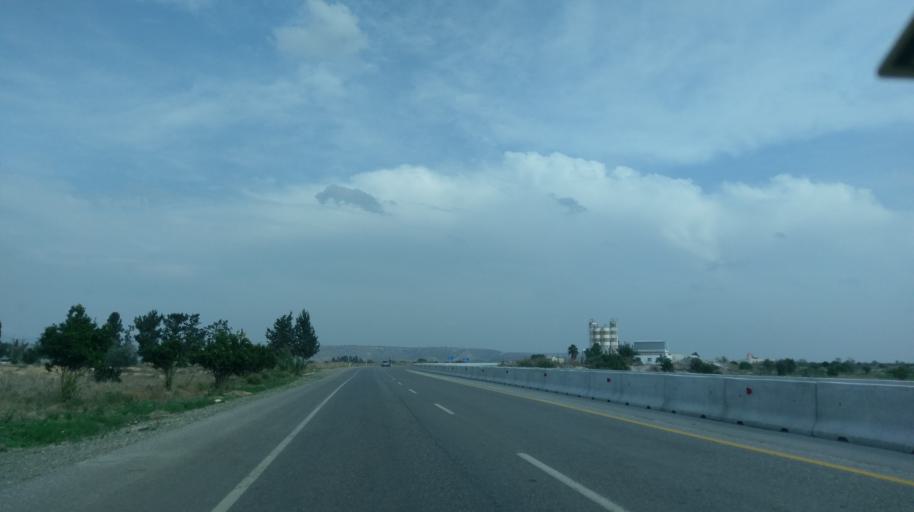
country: CY
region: Lefkosia
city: Morfou
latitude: 35.2019
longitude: 33.0354
